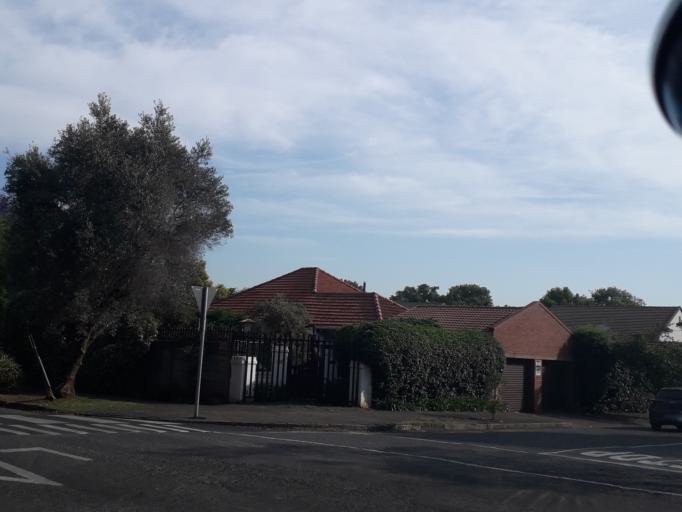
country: ZA
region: Gauteng
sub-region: City of Johannesburg Metropolitan Municipality
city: Johannesburg
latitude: -26.1560
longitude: 28.0233
